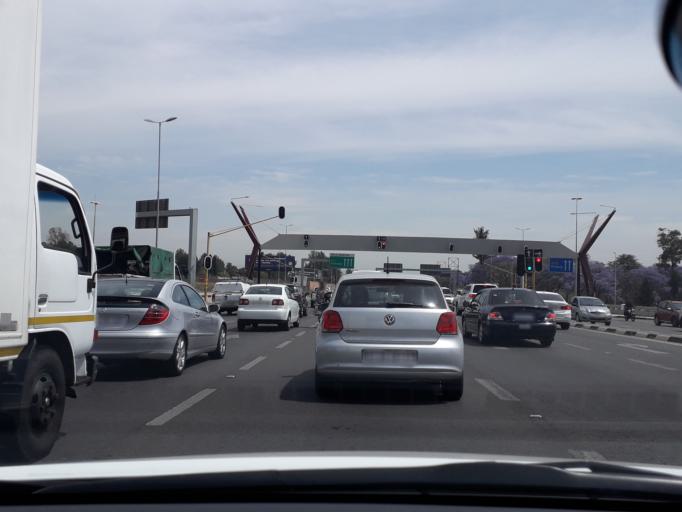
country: ZA
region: Gauteng
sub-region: City of Johannesburg Metropolitan Municipality
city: Diepsloot
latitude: -26.0395
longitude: 28.0135
